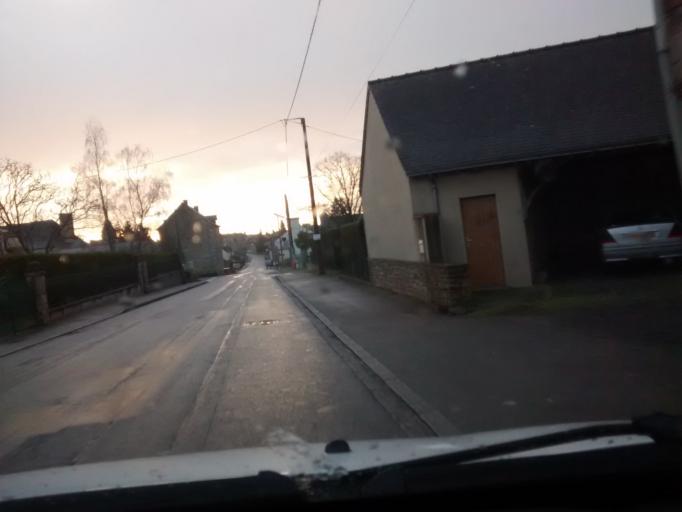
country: FR
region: Brittany
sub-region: Departement d'Ille-et-Vilaine
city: Bais
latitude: 48.0123
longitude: -1.2942
